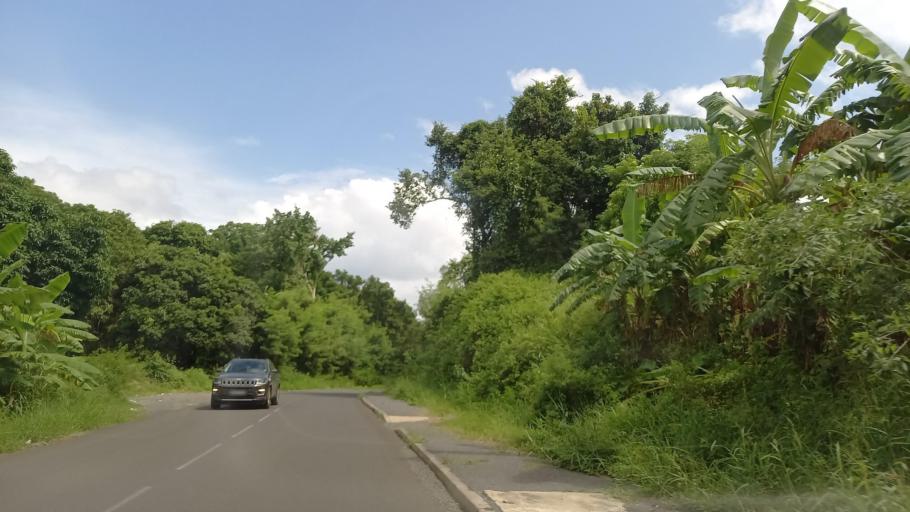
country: YT
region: Boueni
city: Boueni
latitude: -12.9240
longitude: 45.0948
